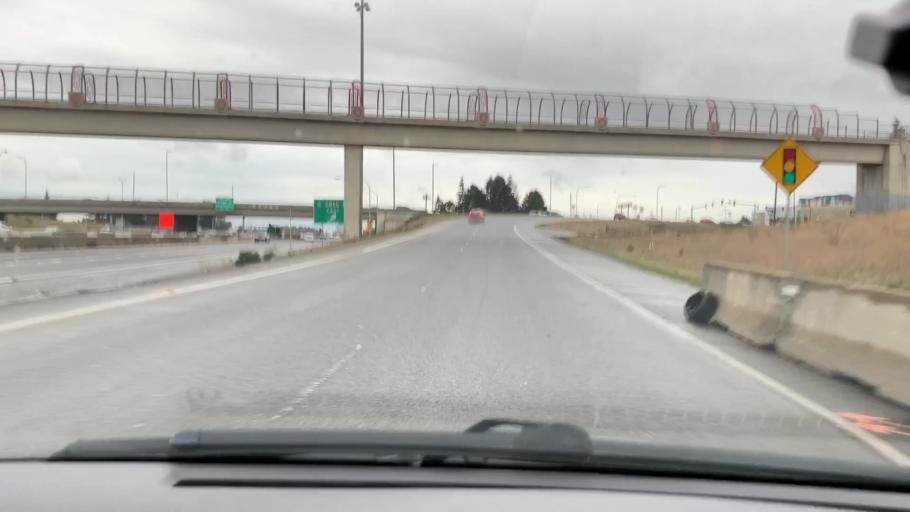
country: US
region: Washington
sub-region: Pierce County
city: Tacoma
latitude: 47.2248
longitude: -122.4640
